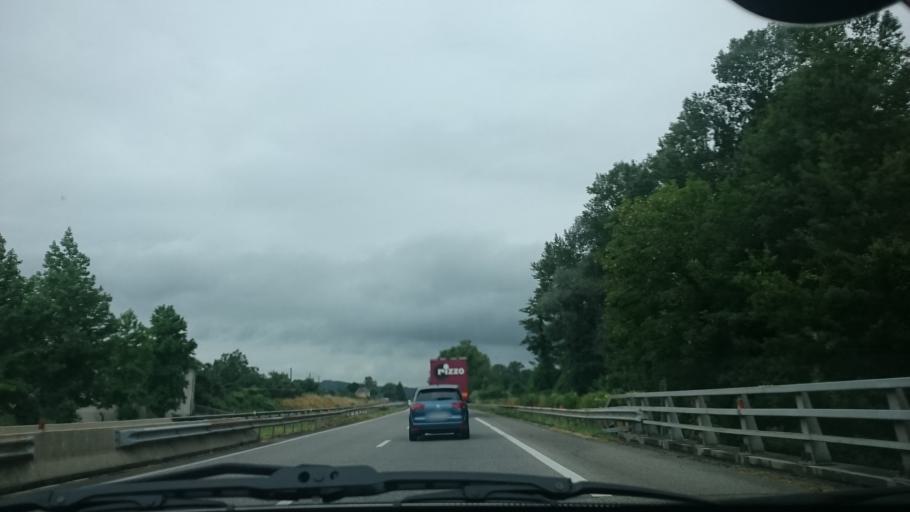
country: FR
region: Aquitaine
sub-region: Departement des Pyrenees-Atlantiques
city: Mont
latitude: 43.4580
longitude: -0.7083
